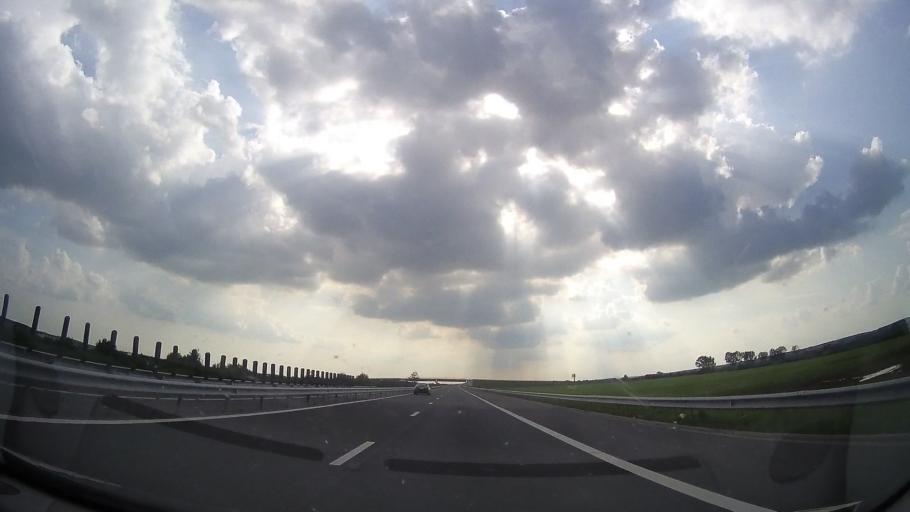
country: RO
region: Timis
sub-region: Comuna Bethausen
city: Bethausen
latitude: 45.8058
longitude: 21.9086
